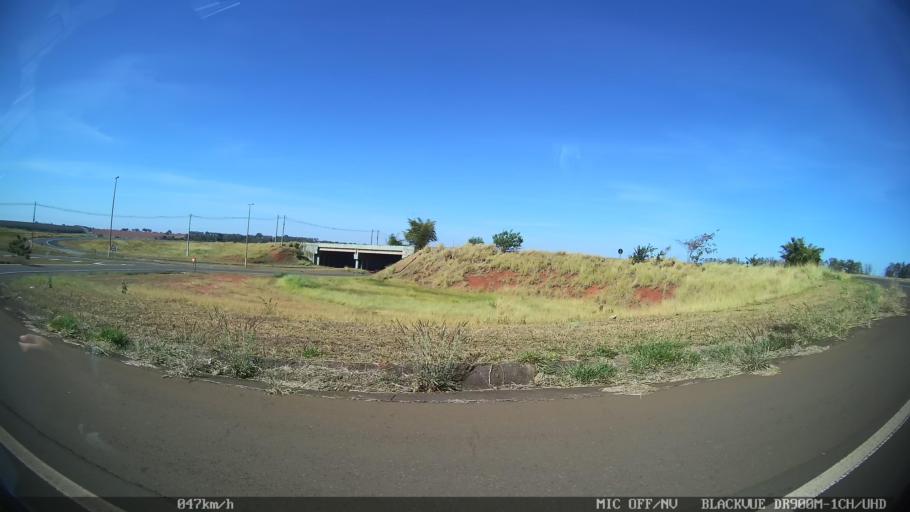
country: BR
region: Sao Paulo
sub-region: Barretos
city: Barretos
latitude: -20.5271
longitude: -48.5914
